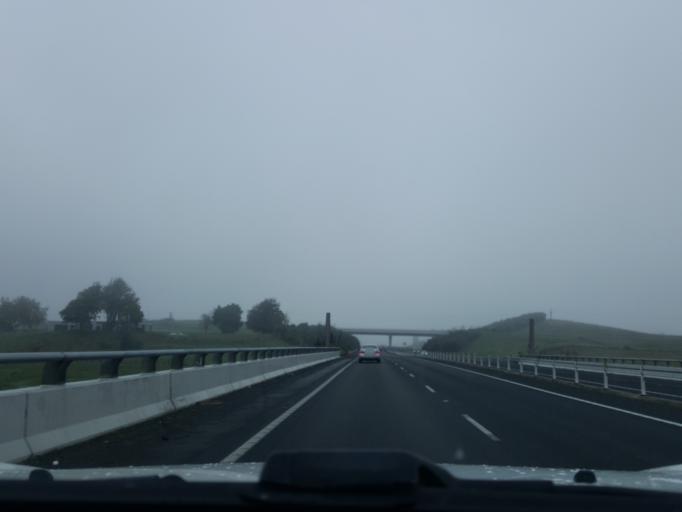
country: NZ
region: Waikato
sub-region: Waikato District
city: Ngaruawahia
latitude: -37.6996
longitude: 175.2107
